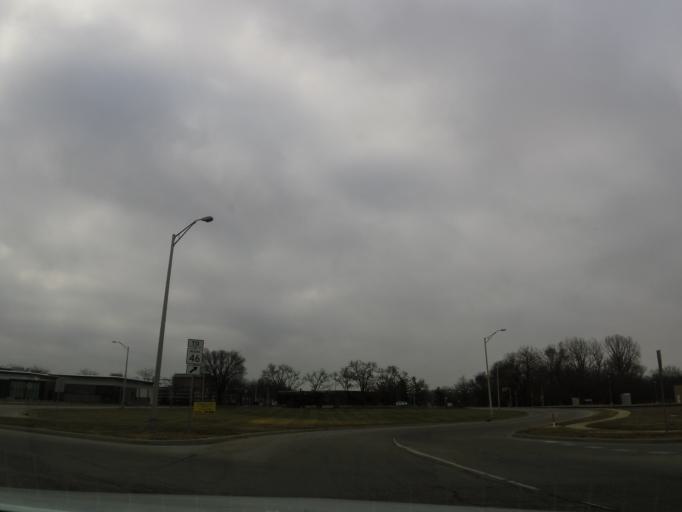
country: US
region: Indiana
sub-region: Bartholomew County
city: Columbus
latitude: 39.2084
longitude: -85.9246
